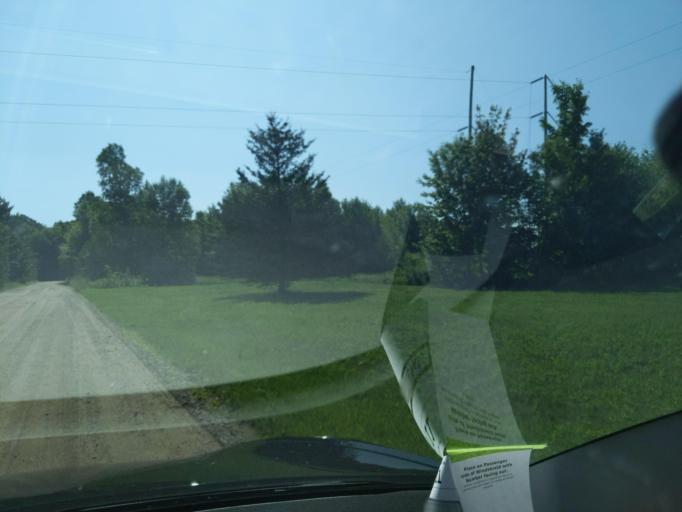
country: US
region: Michigan
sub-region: Cheboygan County
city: Cheboygan
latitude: 45.6791
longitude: -84.6533
